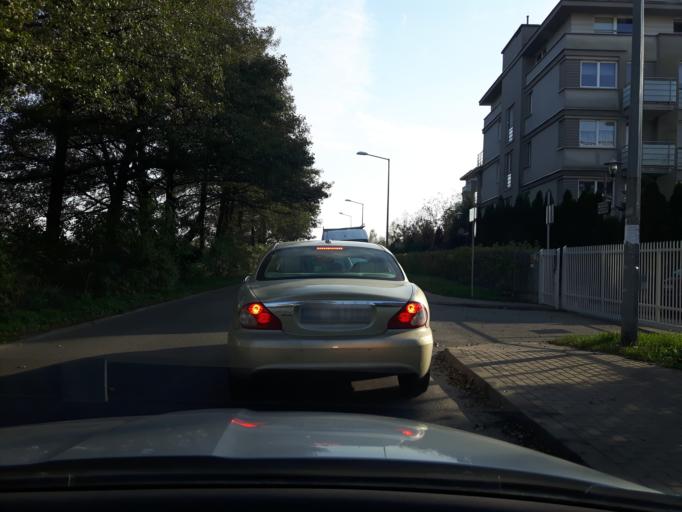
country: PL
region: Masovian Voivodeship
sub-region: Warszawa
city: Targowek
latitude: 52.3108
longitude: 21.0728
